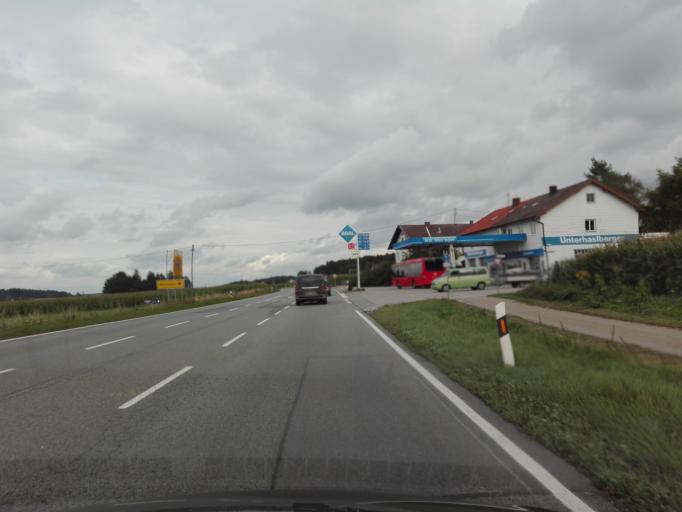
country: DE
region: Bavaria
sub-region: Upper Bavaria
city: Maitenbeth
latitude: 48.1537
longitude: 12.0912
